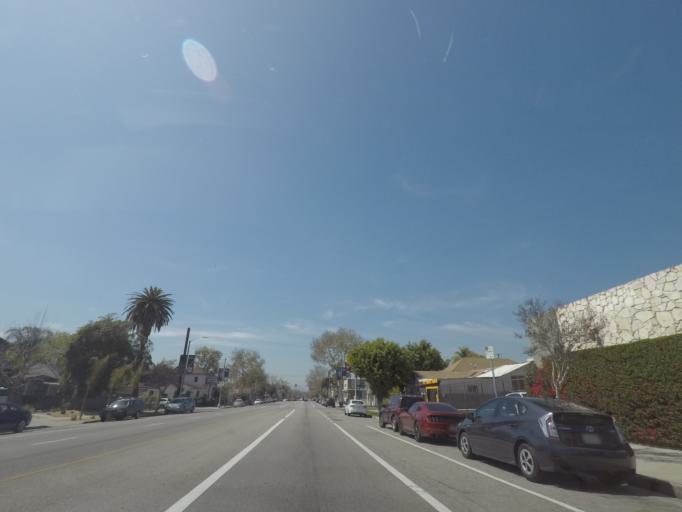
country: US
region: California
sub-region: Los Angeles County
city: South Pasadena
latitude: 34.1185
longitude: -118.1916
